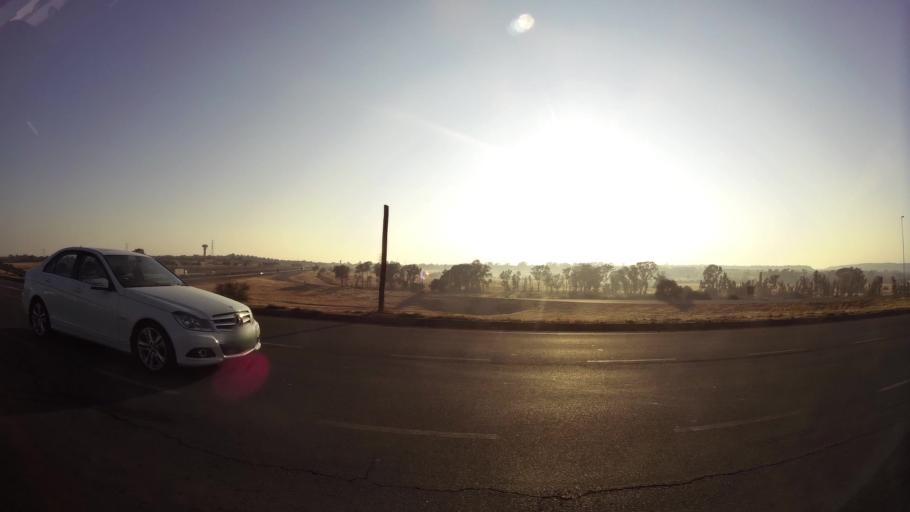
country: ZA
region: Orange Free State
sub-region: Mangaung Metropolitan Municipality
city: Bloemfontein
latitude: -29.0909
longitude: 26.1720
